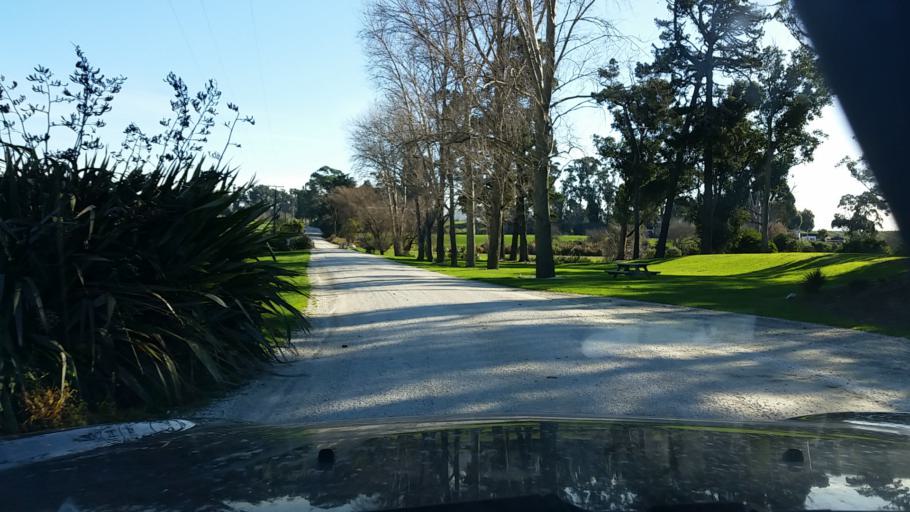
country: NZ
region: Marlborough
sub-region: Marlborough District
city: Blenheim
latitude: -41.6519
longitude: 174.1349
